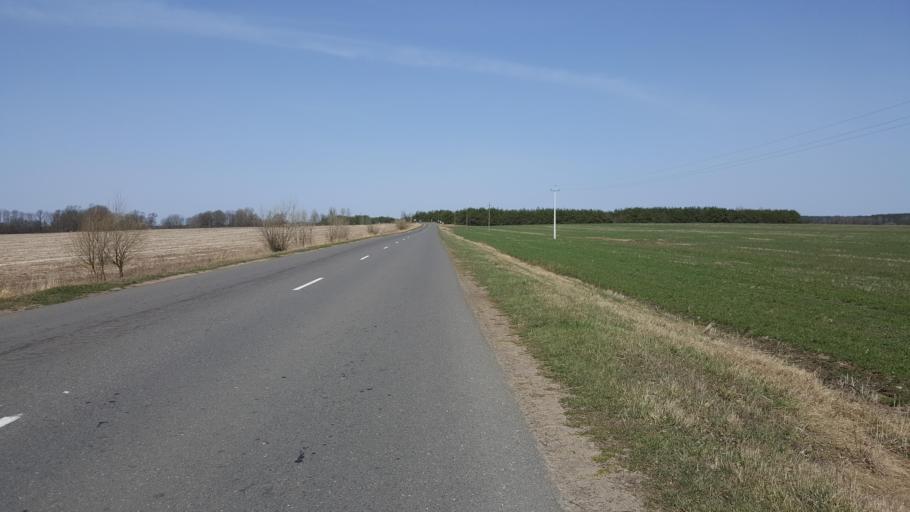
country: BY
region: Brest
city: Kamyanyuki
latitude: 52.4857
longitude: 23.6948
